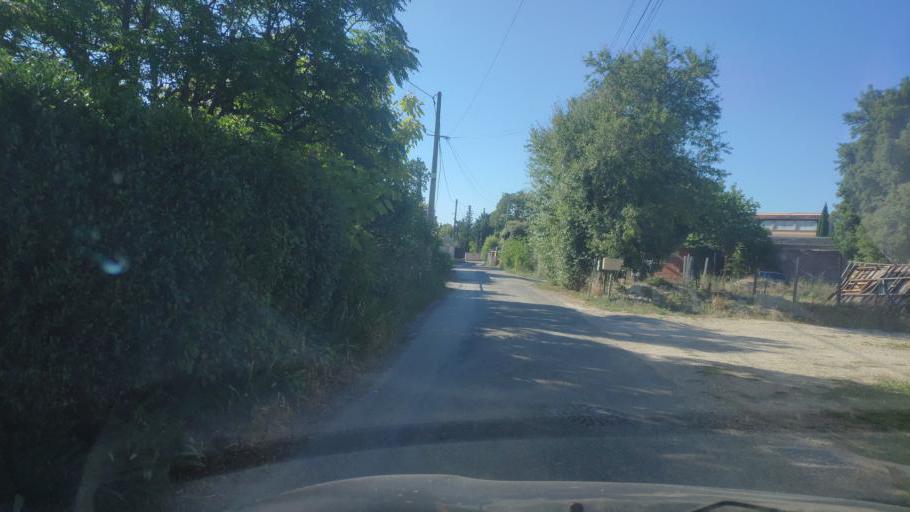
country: FR
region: Provence-Alpes-Cote d'Azur
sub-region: Departement du Vaucluse
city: Carpentras
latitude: 44.0745
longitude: 5.0483
